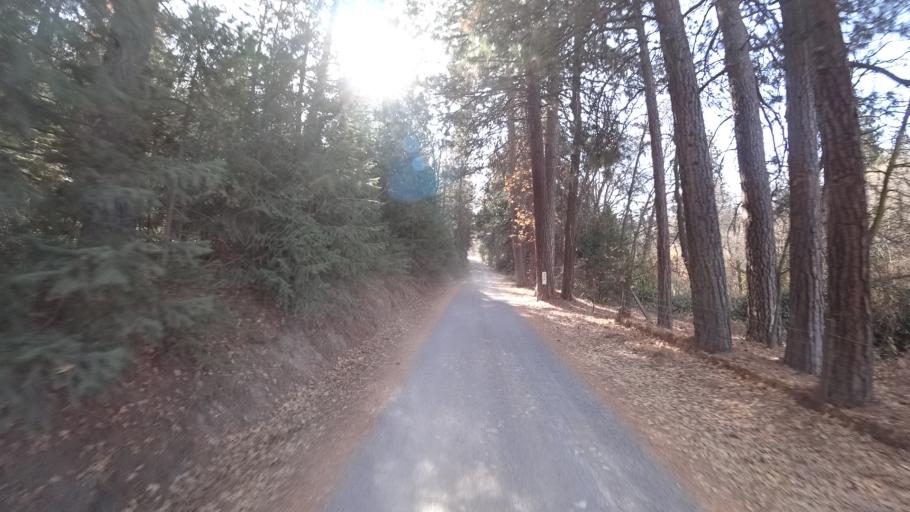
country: US
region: California
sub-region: Siskiyou County
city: Weed
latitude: 41.4419
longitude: -122.4244
